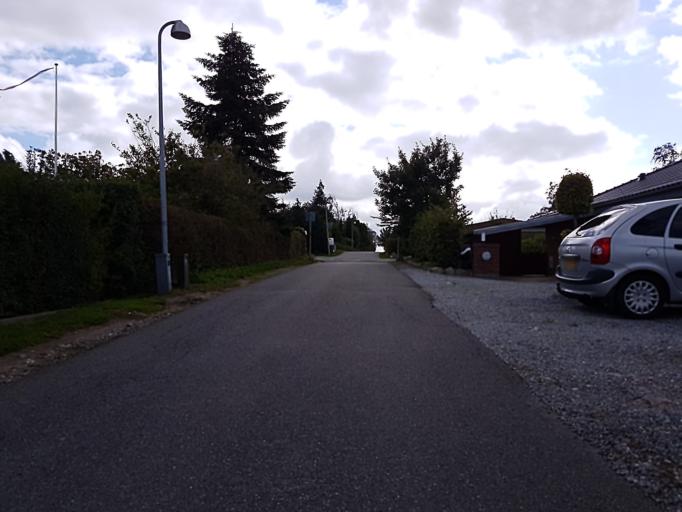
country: DK
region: Zealand
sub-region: Roskilde Kommune
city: Jyllinge
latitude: 55.7624
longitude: 12.1032
